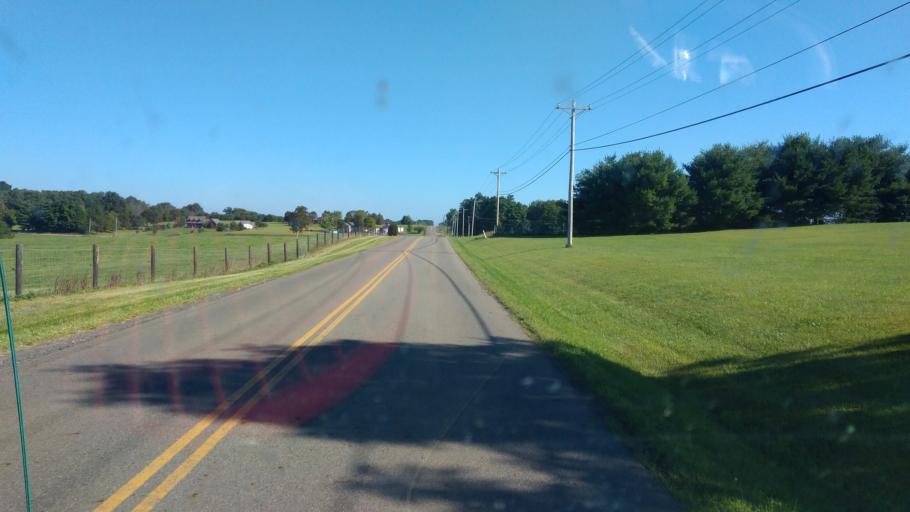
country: US
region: Ohio
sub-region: Knox County
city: Gambier
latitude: 40.4286
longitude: -82.3676
